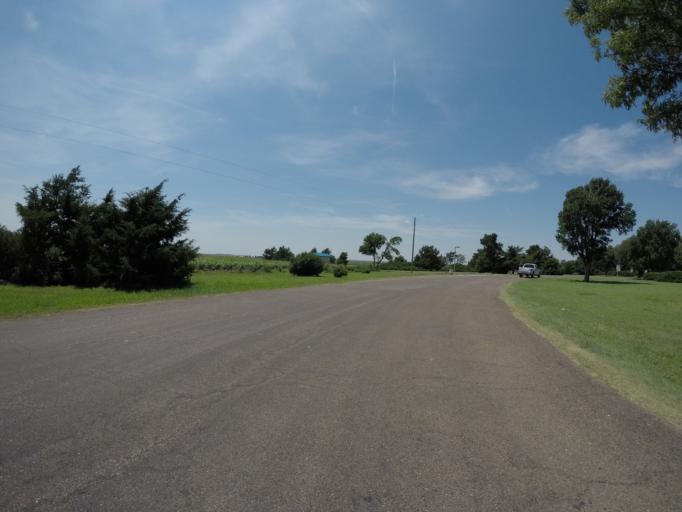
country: US
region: Kansas
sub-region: Gove County
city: Gove
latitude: 39.0983
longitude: -100.4271
